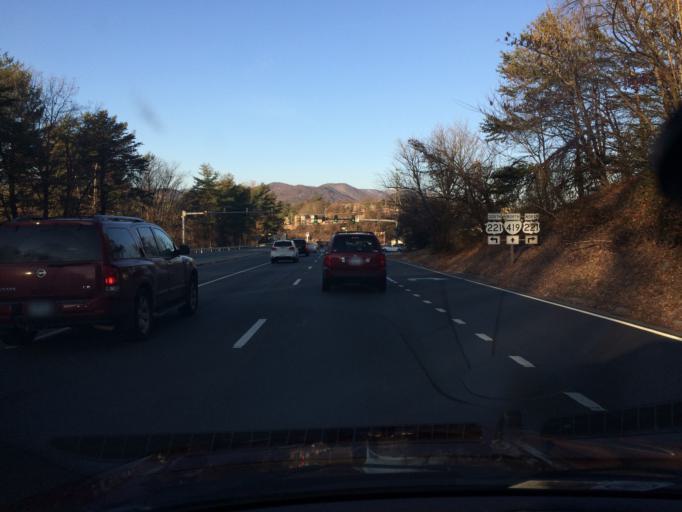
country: US
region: Virginia
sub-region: Roanoke County
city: Cave Spring
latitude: 37.2291
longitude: -80.0047
